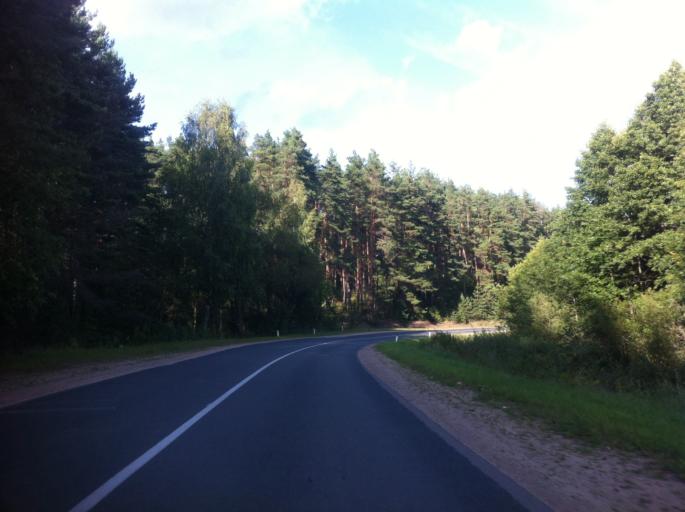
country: RU
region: Pskov
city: Izborsk
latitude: 57.8350
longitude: 27.9208
